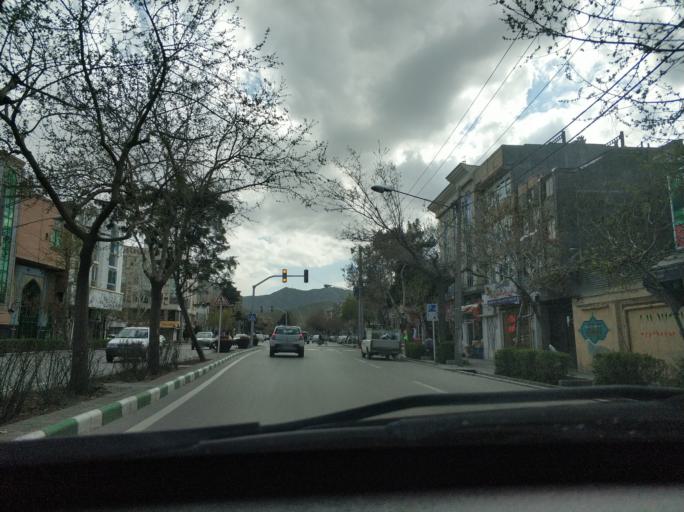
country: IR
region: Razavi Khorasan
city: Mashhad
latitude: 36.2717
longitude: 59.5899
